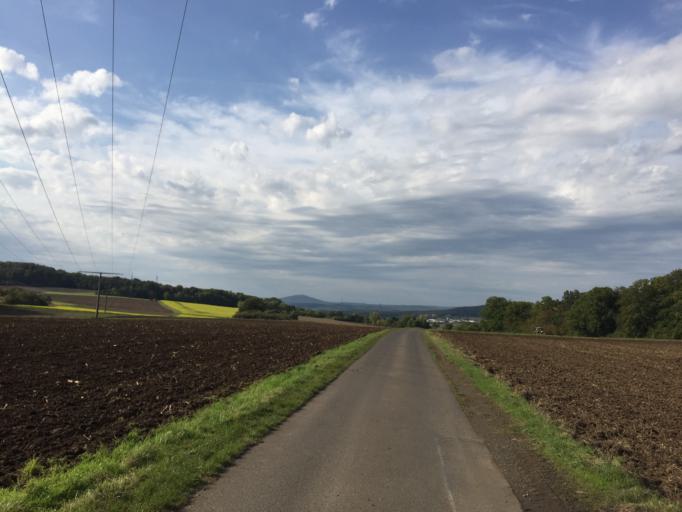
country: DE
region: Hesse
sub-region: Regierungsbezirk Giessen
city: Grossen Buseck
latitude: 50.5963
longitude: 8.7786
